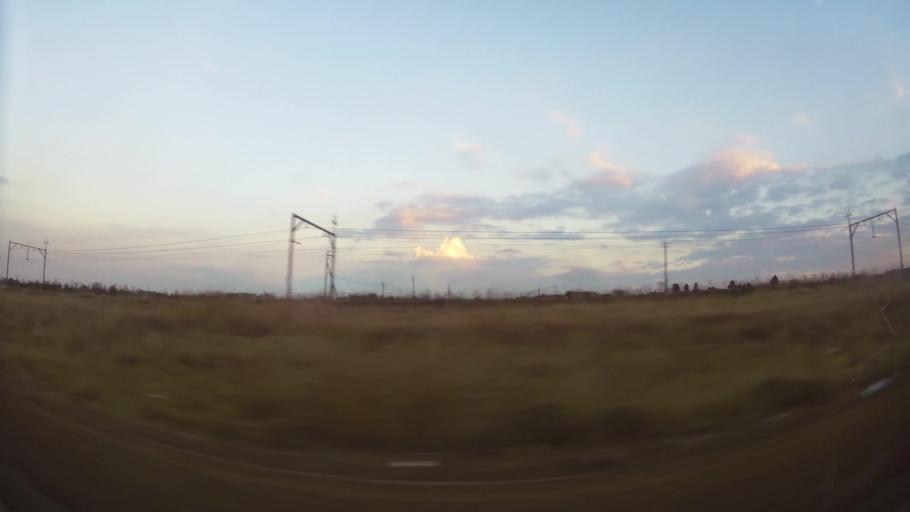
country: ZA
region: Gauteng
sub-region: City of Johannesburg Metropolitan Municipality
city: Orange Farm
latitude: -26.5623
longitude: 27.8711
